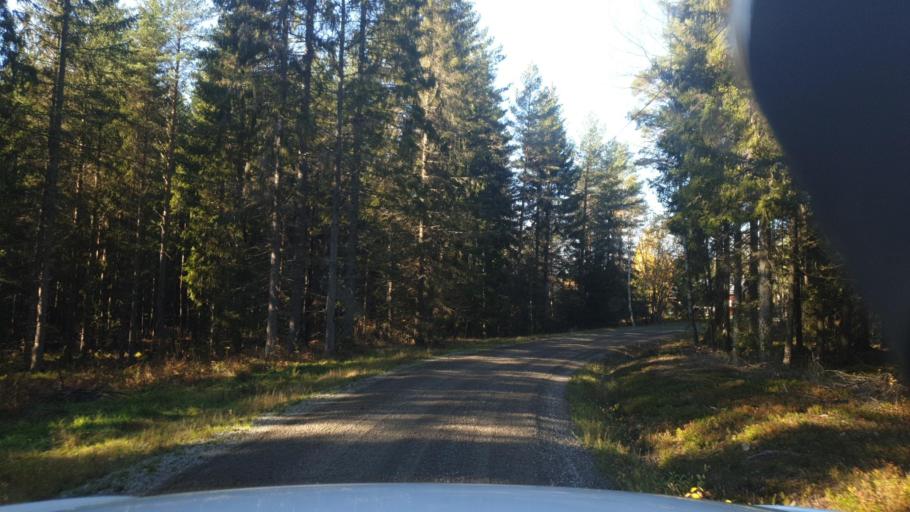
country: SE
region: Vaermland
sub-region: Arvika Kommun
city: Arvika
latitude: 59.5606
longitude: 12.8417
